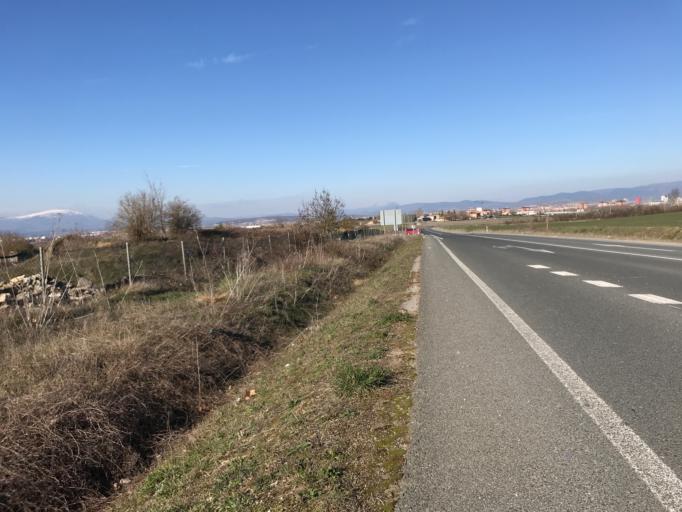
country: ES
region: Basque Country
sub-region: Provincia de Alava
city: Gasteiz / Vitoria
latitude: 42.8151
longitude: -2.6807
